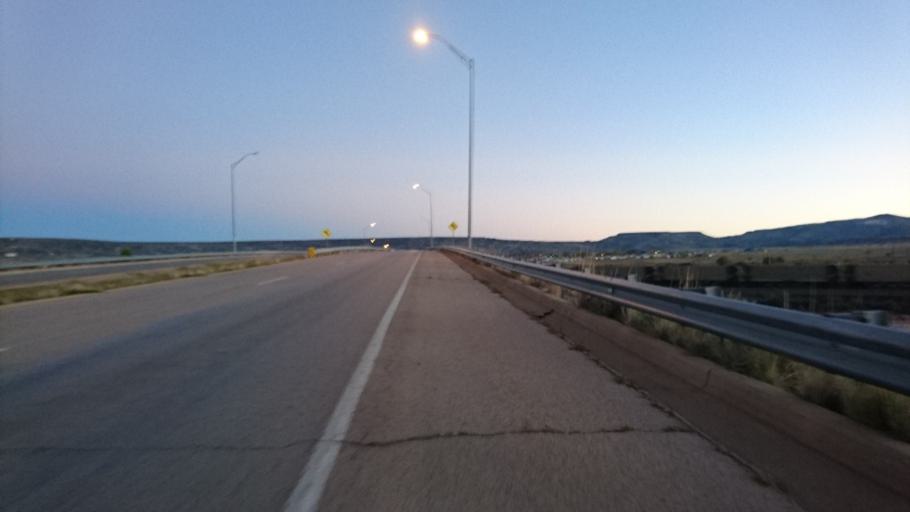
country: US
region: New Mexico
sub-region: Cibola County
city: Grants
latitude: 35.1357
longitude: -107.8277
